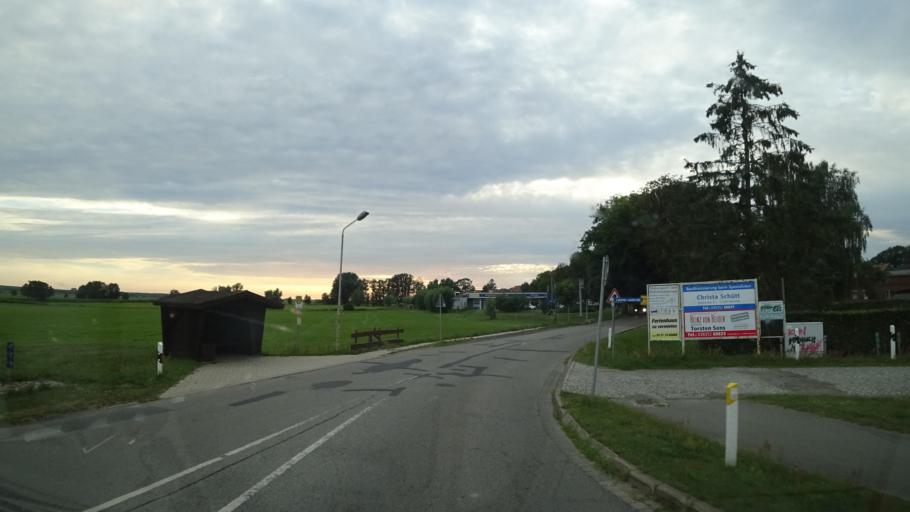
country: DE
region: Mecklenburg-Vorpommern
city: Kemnitz
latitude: 54.0840
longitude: 13.5358
